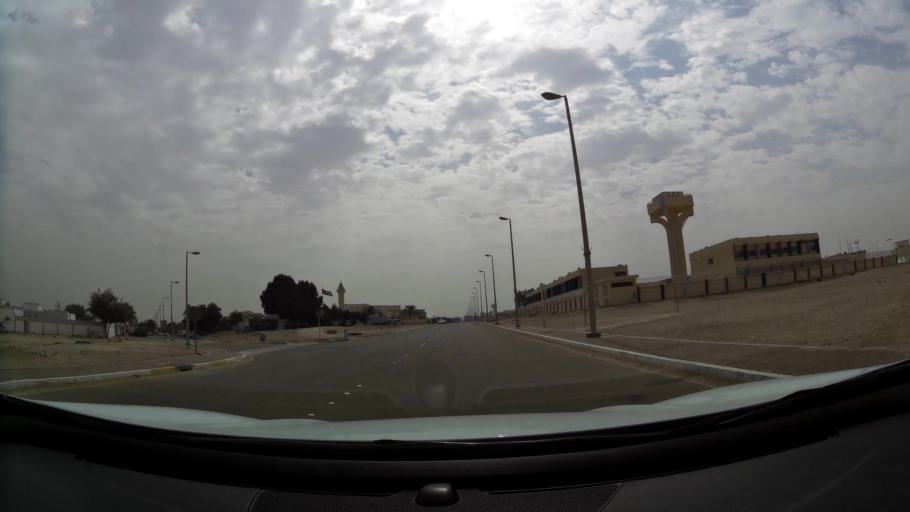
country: AE
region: Abu Dhabi
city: Abu Dhabi
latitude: 24.3196
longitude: 54.6397
